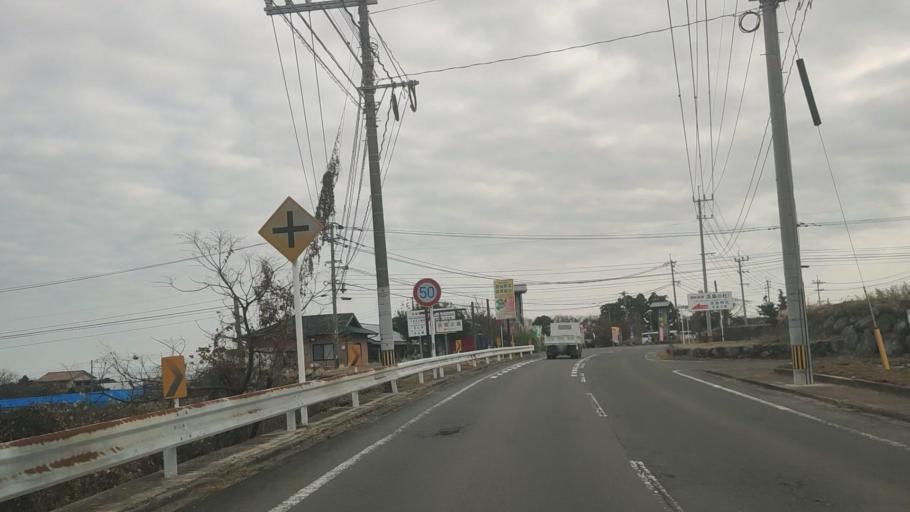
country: JP
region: Nagasaki
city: Shimabara
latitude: 32.8532
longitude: 130.2730
